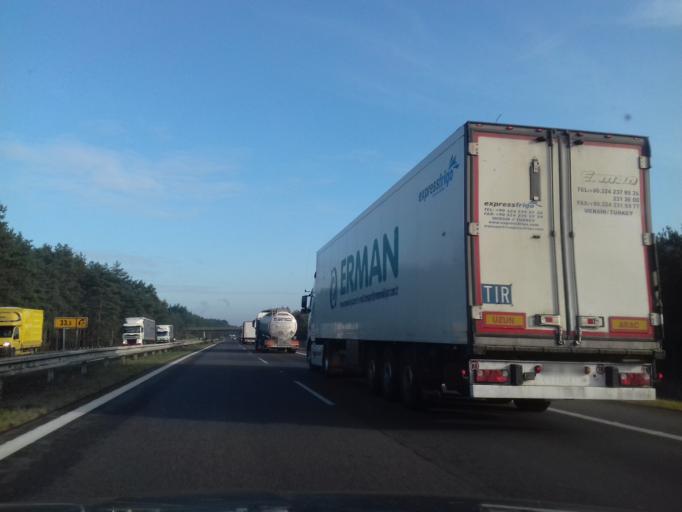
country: SK
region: Bratislavsky
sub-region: Okres Malacky
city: Malacky
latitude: 48.3923
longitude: 17.0255
